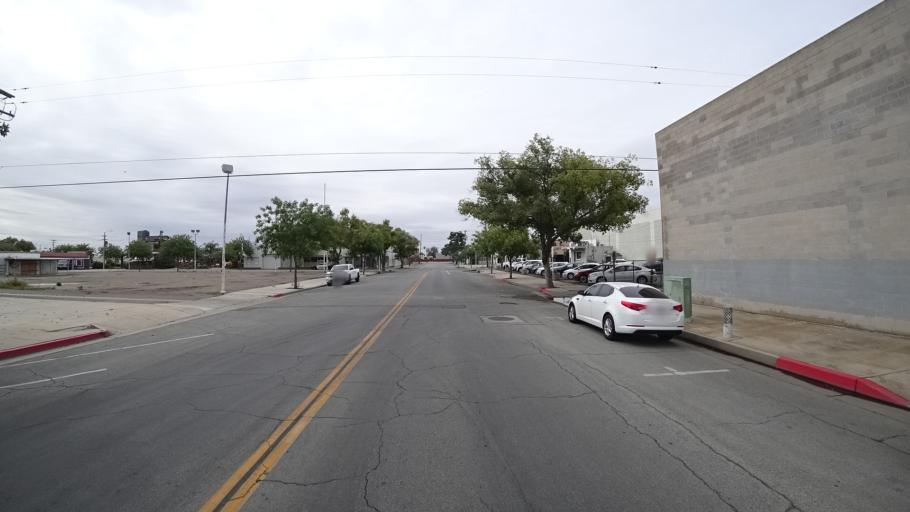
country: US
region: California
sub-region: Kings County
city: Hanford
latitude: 36.3276
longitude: -119.6443
